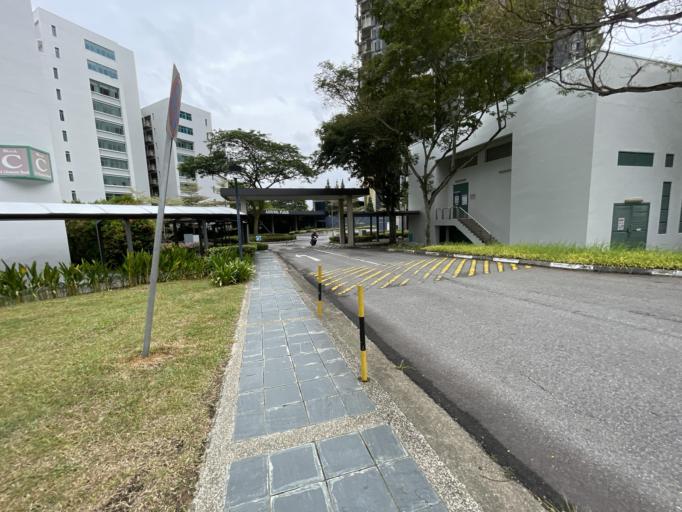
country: SG
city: Singapore
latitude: 1.3018
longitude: 103.7689
